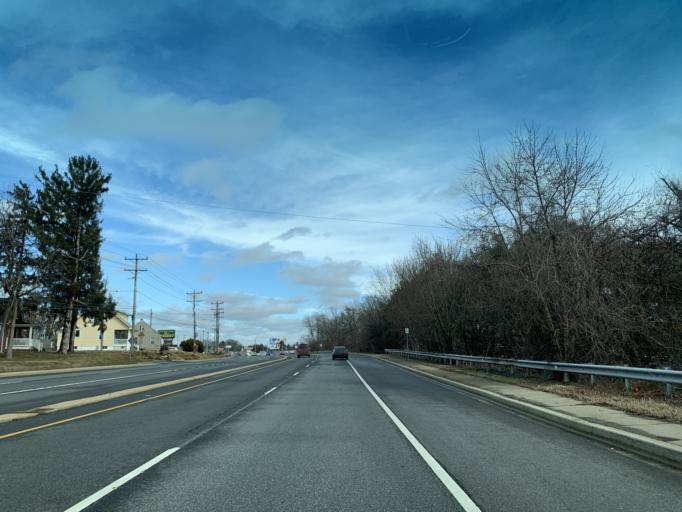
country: US
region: Delaware
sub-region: New Castle County
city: Pike Creek
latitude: 39.7043
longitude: -75.6893
